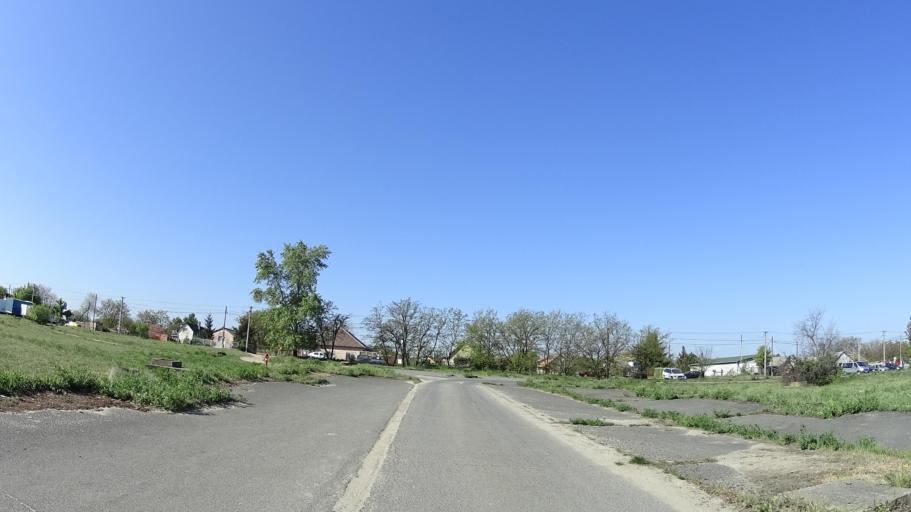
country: HU
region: Budapest
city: Budapest XXIII. keruelet
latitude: 47.4146
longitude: 19.1300
